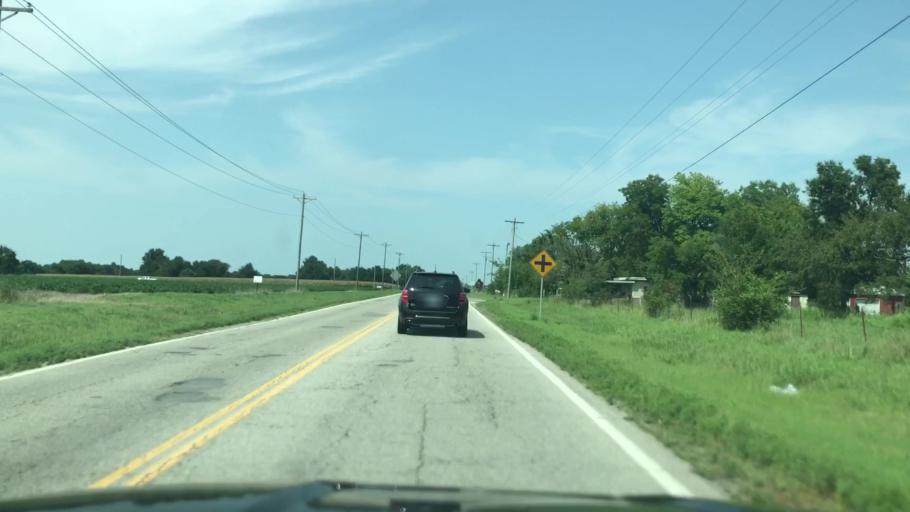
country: US
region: Oklahoma
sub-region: Ottawa County
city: Miami
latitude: 36.8979
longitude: -94.8418
